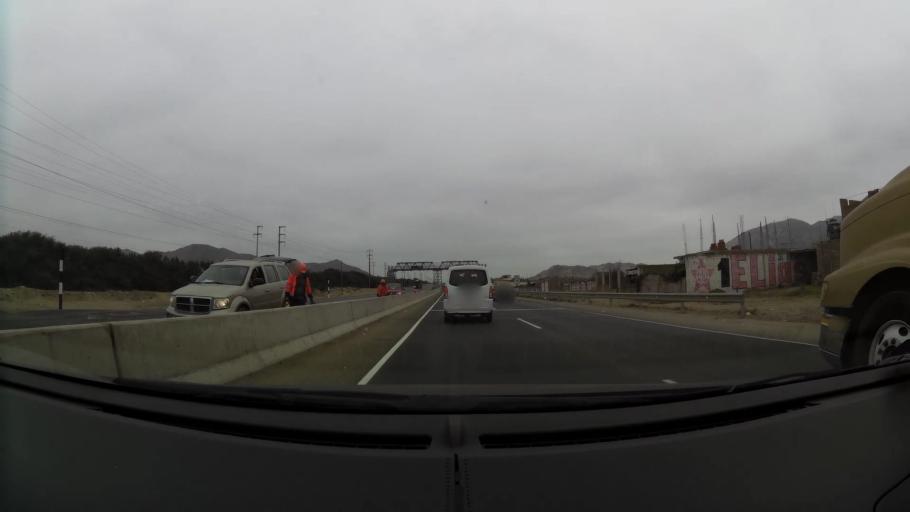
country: PE
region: La Libertad
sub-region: Viru
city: Chao
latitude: -8.5101
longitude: -78.6872
